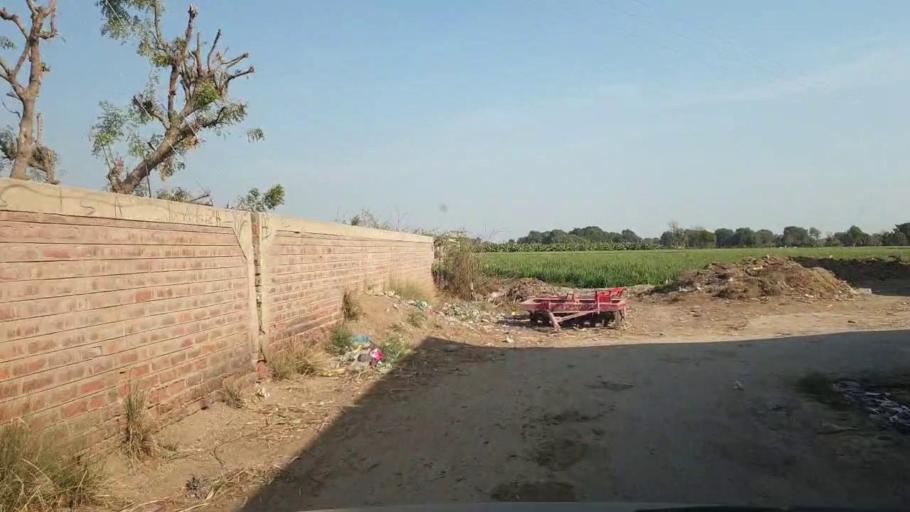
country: PK
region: Sindh
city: Chambar
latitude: 25.3371
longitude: 68.7494
